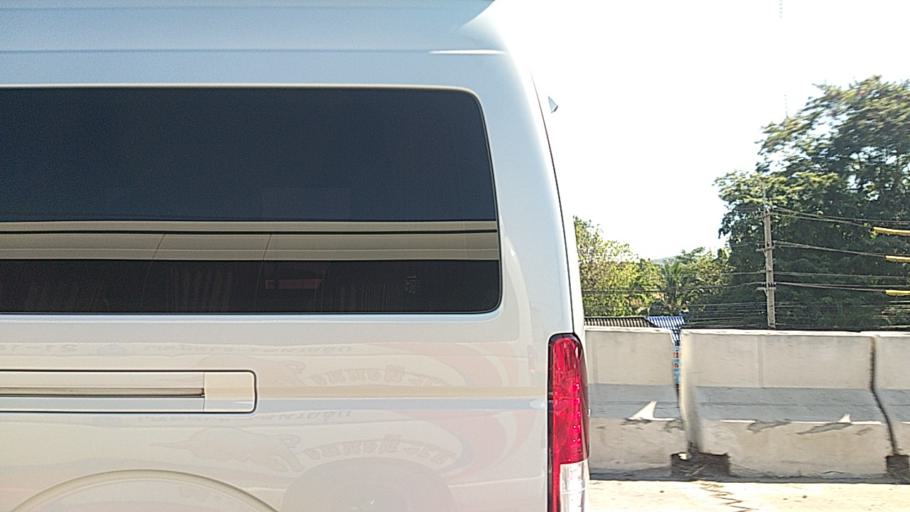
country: TH
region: Sara Buri
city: Saraburi
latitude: 14.5188
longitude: 100.9149
